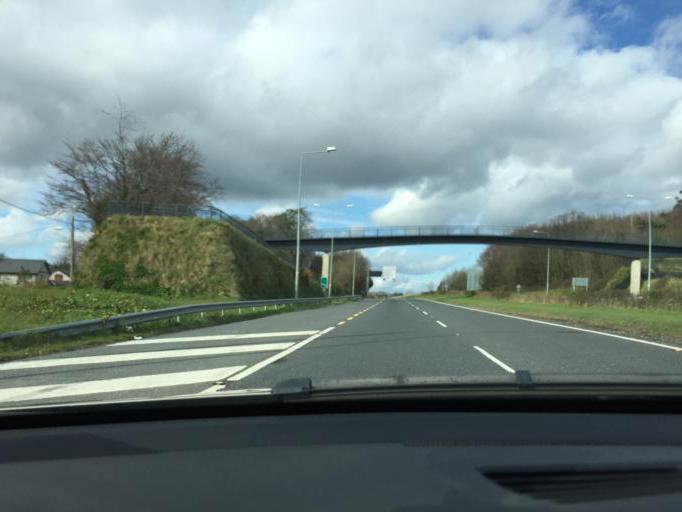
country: IE
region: Leinster
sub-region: Wicklow
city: Kilpedder
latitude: 53.1106
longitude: -6.1054
